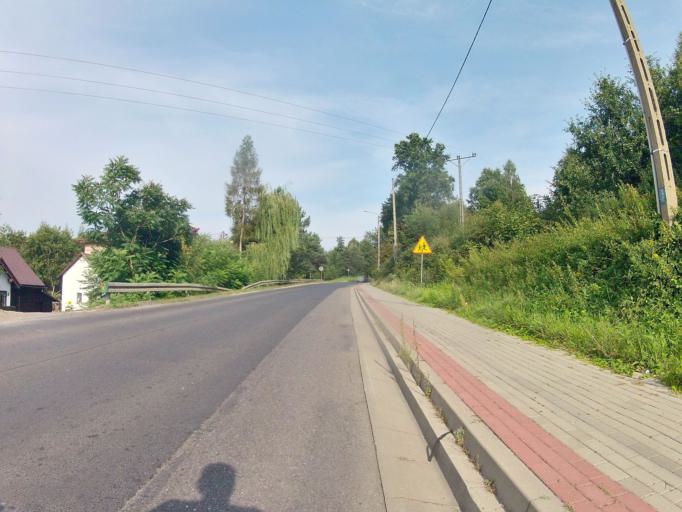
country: PL
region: Subcarpathian Voivodeship
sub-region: Powiat jasielski
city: Jaslo
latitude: 49.7548
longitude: 21.4456
